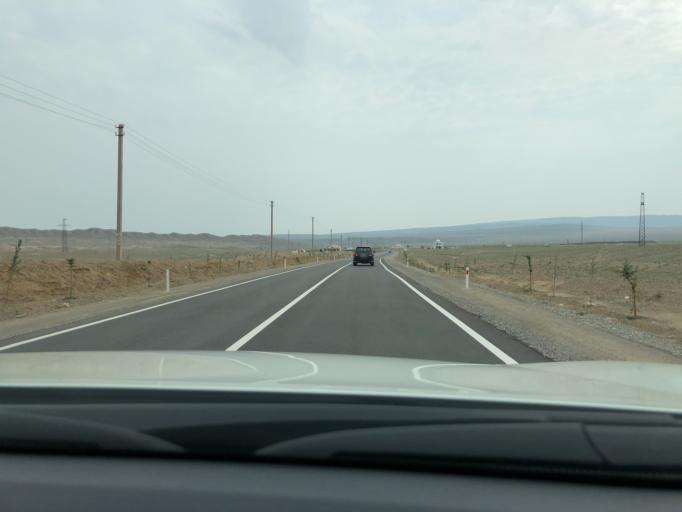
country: TJ
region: Viloyati Sughd
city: Kim
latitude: 40.1970
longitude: 70.4760
